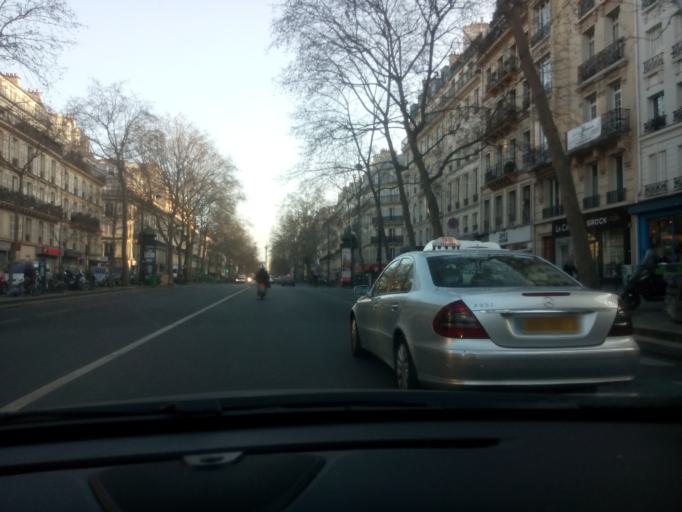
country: FR
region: Ile-de-France
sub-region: Paris
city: Paris
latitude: 48.8594
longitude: 2.3675
